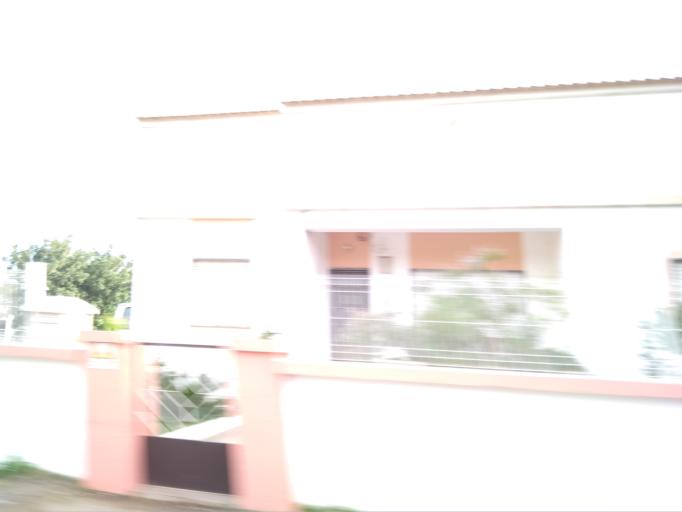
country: PT
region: Faro
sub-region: Faro
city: Santa Barbara de Nexe
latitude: 37.0919
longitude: -7.9167
